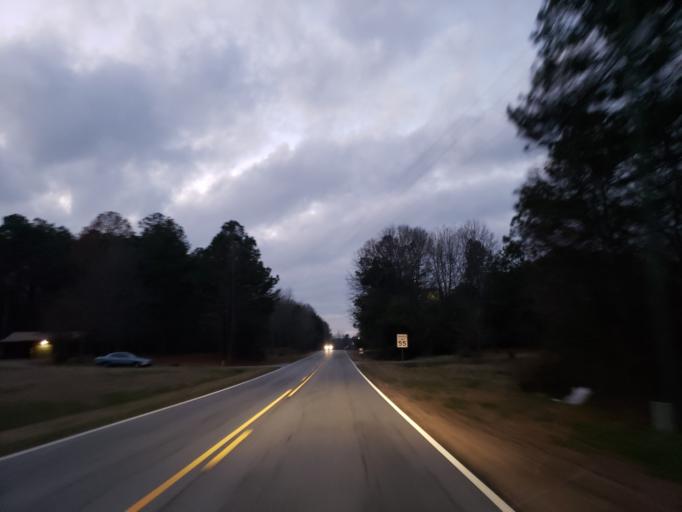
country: US
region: Georgia
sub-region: Carroll County
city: Temple
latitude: 33.7689
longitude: -85.0533
